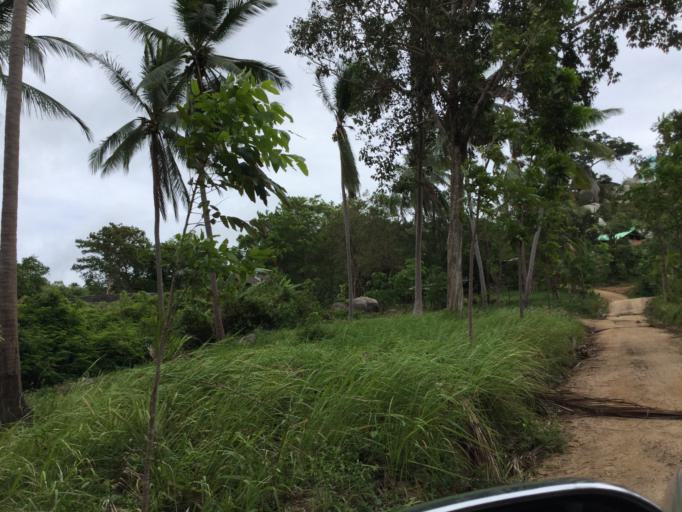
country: TH
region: Nakhon Si Thammarat
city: Ko Pha Ngan
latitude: 9.7370
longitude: 100.0756
